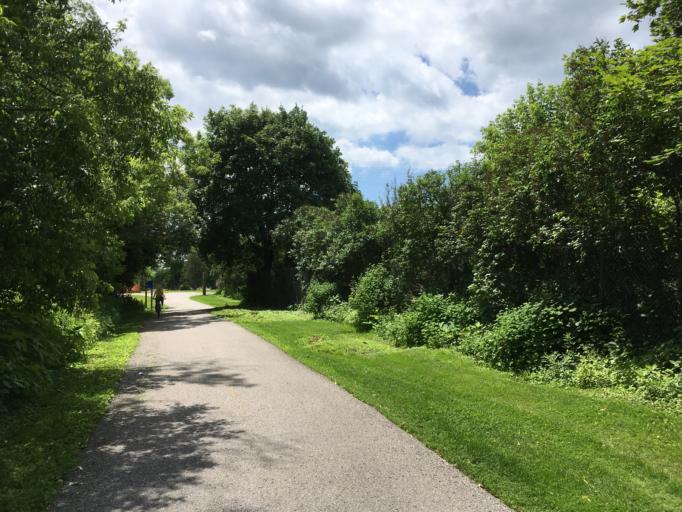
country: CA
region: Ontario
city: Oshawa
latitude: 43.8902
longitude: -78.8656
